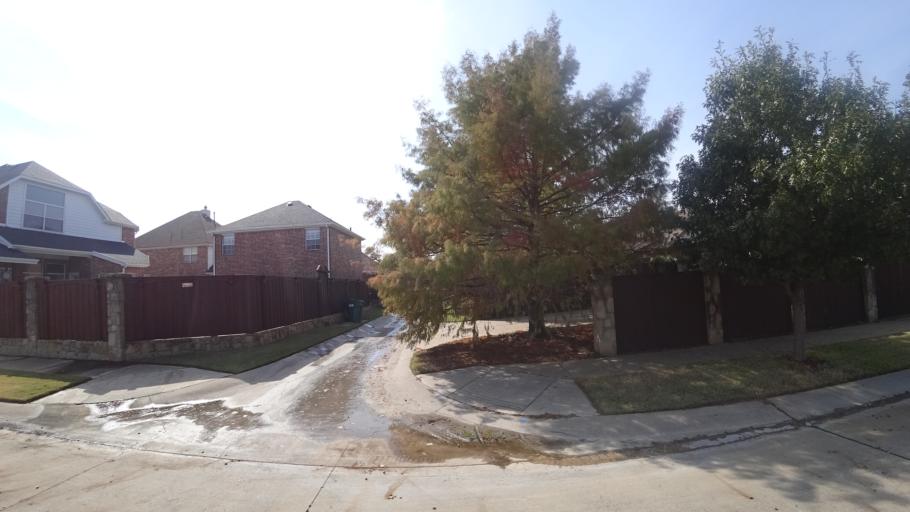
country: US
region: Texas
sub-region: Denton County
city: The Colony
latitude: 33.0319
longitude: -96.8938
